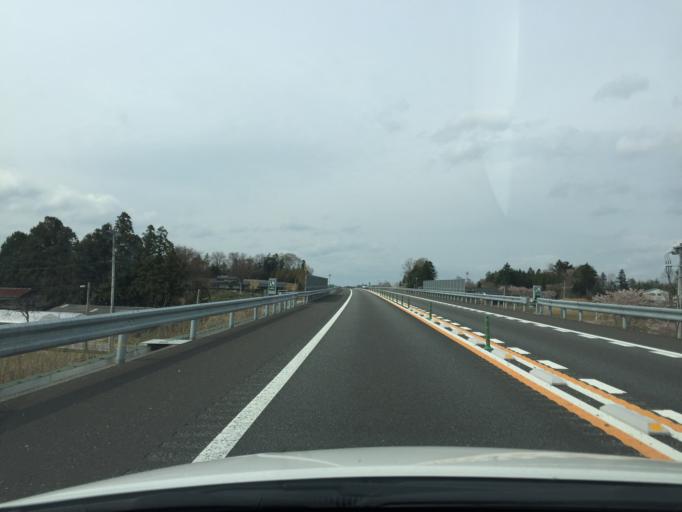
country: JP
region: Fukushima
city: Namie
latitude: 37.5617
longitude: 140.9454
